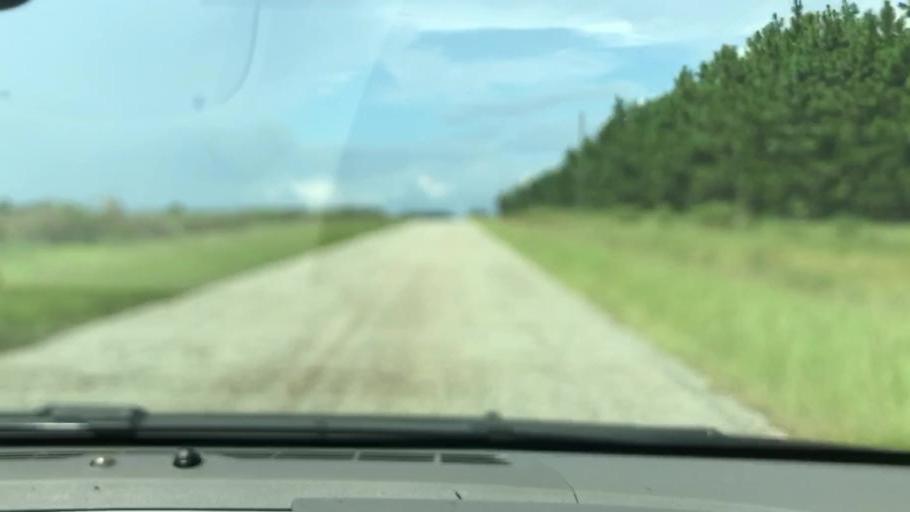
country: US
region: Georgia
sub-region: Seminole County
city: Donalsonville
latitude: 31.1770
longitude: -85.0045
